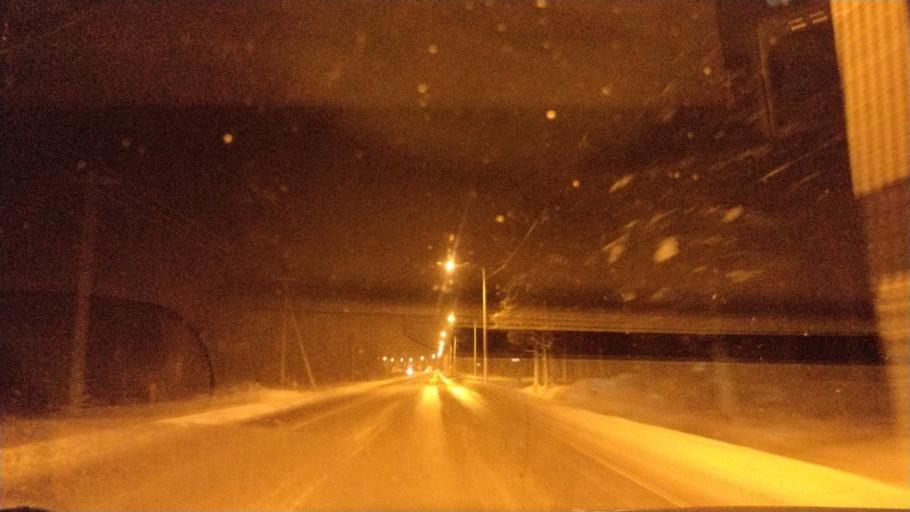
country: FI
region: Lapland
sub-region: Rovaniemi
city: Rovaniemi
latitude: 66.3055
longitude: 25.3576
